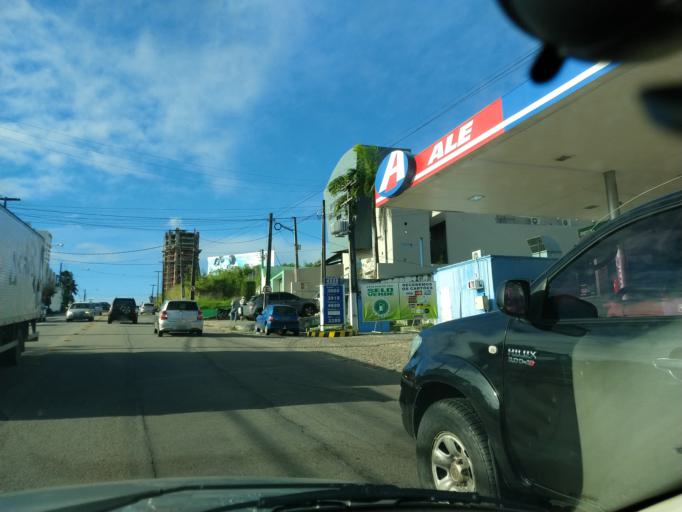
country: BR
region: Rio Grande do Norte
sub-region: Natal
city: Natal
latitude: -5.8317
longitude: -35.2229
